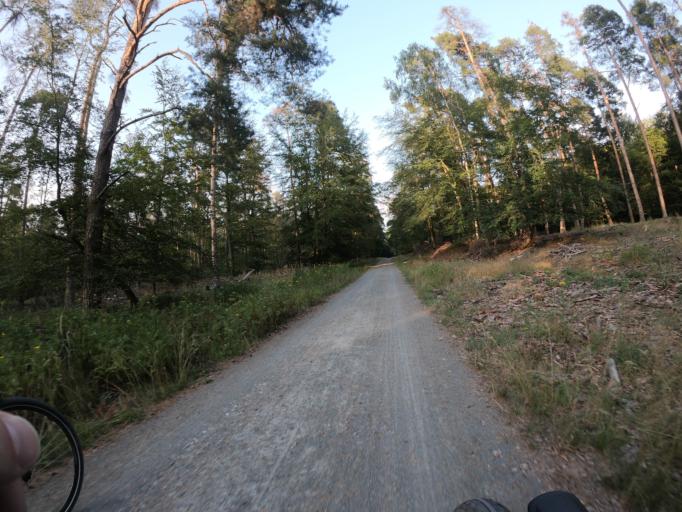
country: DE
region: Hesse
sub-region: Regierungsbezirk Darmstadt
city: Gross-Gerau
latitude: 49.9653
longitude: 8.5177
